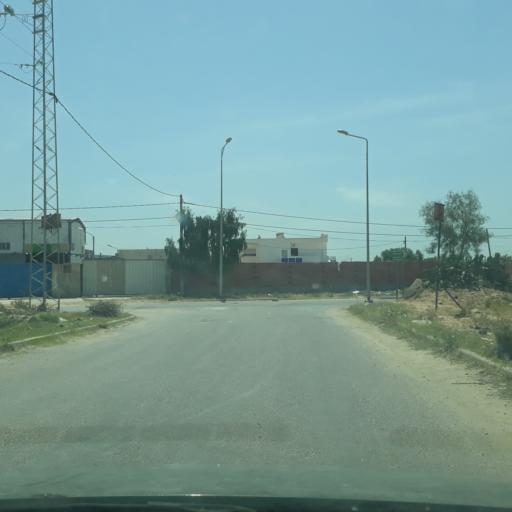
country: TN
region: Safaqis
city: Al Qarmadah
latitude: 34.8242
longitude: 10.7864
